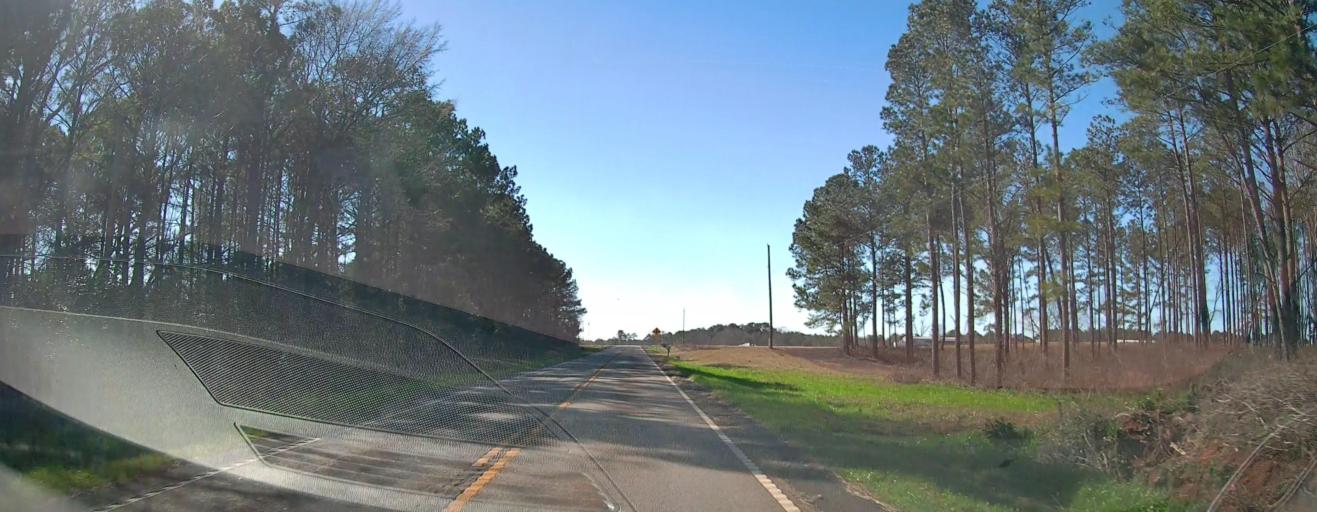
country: US
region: Georgia
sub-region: Schley County
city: Ellaville
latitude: 32.1891
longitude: -84.2014
